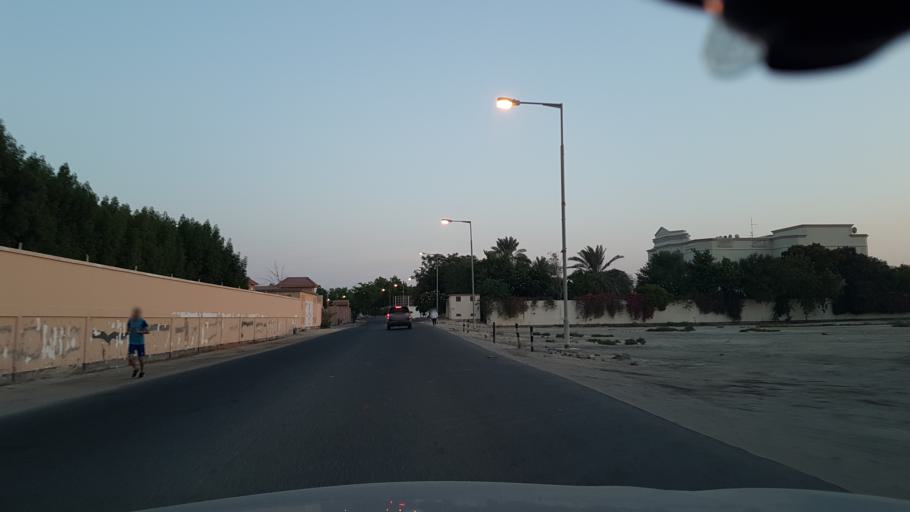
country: BH
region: Manama
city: Jidd Hafs
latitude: 26.2293
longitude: 50.4889
